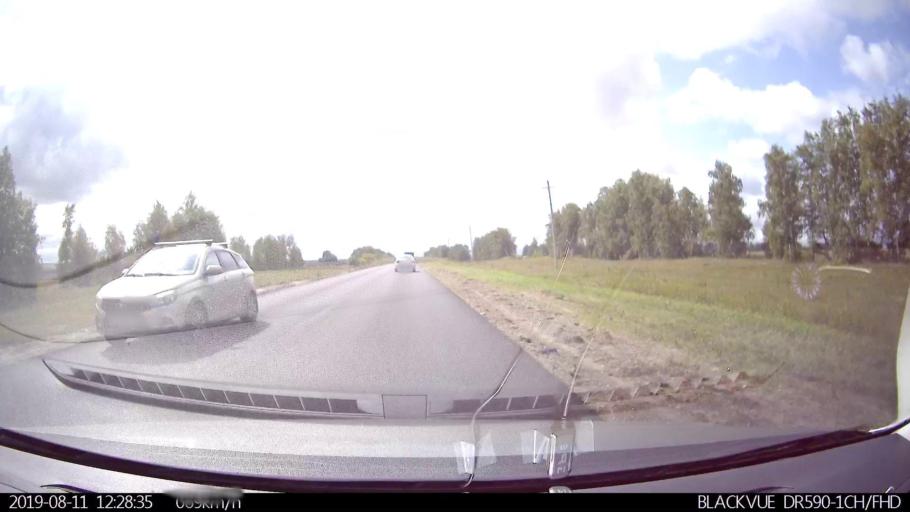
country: RU
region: Ulyanovsk
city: Ignatovka
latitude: 53.8426
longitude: 47.9105
